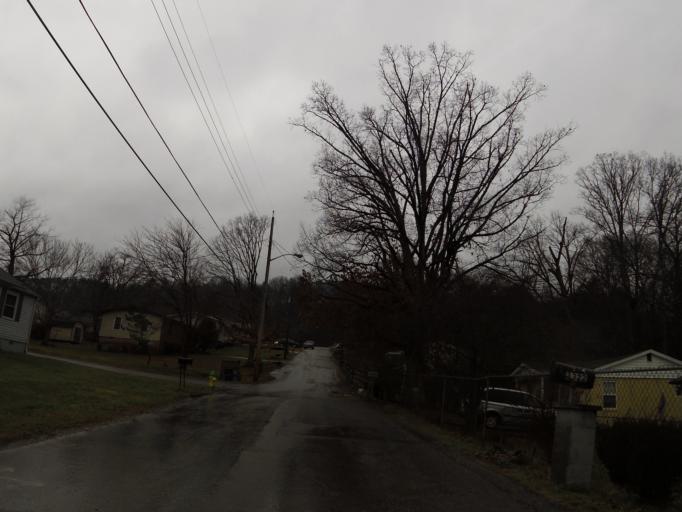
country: US
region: Tennessee
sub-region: Knox County
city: Knoxville
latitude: 35.9828
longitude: -83.9655
